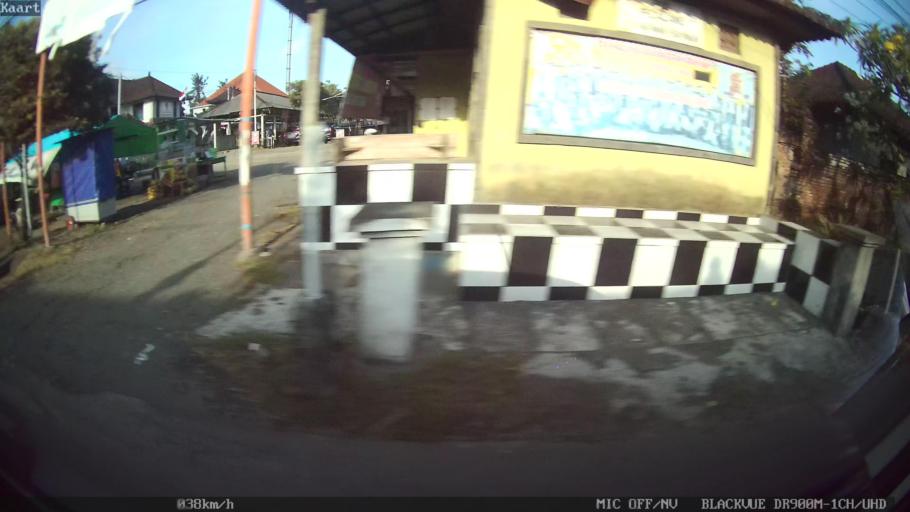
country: ID
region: Bali
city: Banjar Batur
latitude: -8.6014
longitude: 115.2143
